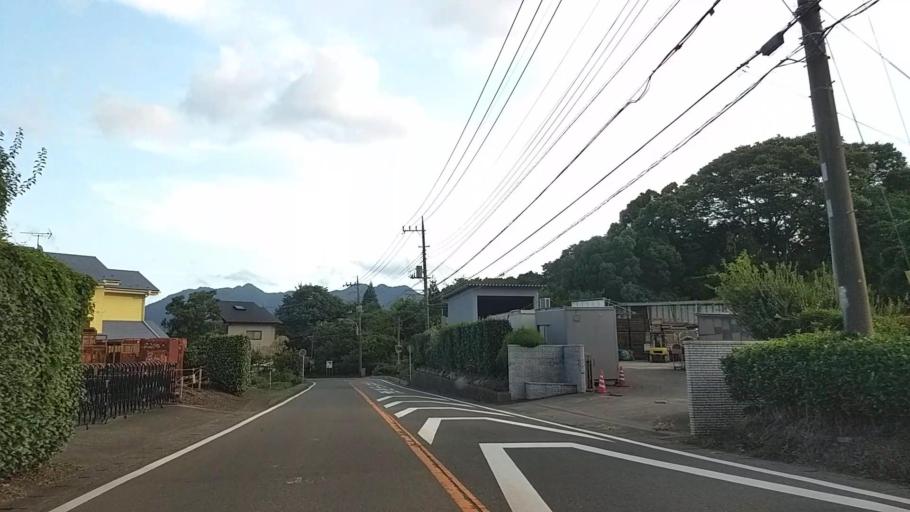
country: JP
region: Tokyo
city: Hachioji
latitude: 35.5715
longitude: 139.2629
